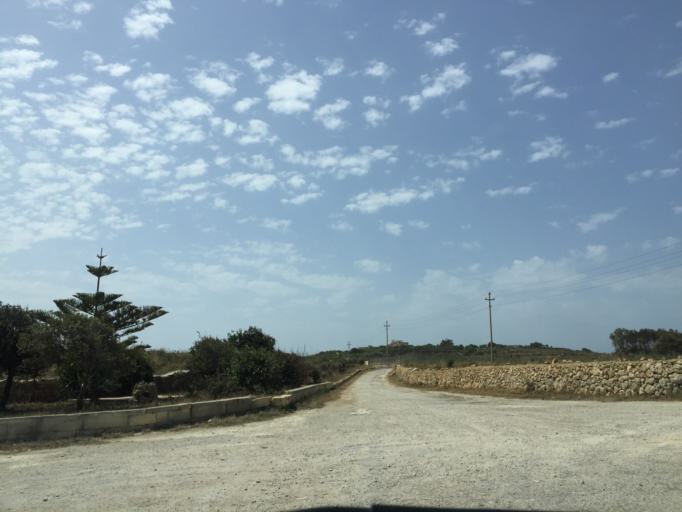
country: MT
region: In-Nadur
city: Nadur
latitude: 36.0540
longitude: 14.2944
